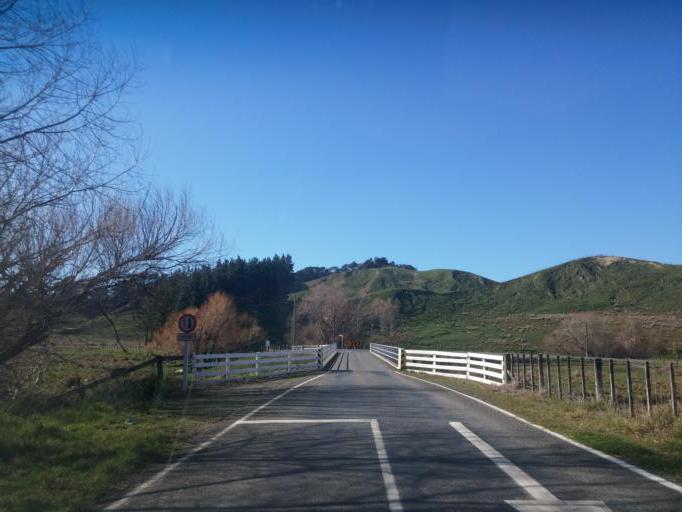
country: NZ
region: Wellington
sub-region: South Wairarapa District
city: Waipawa
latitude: -41.3878
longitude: 175.5140
